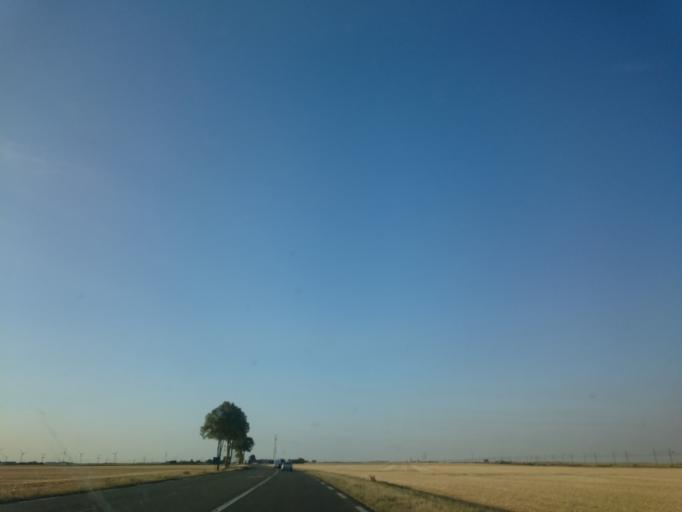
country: FR
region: Centre
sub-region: Departement d'Eure-et-Loir
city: Toury
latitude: 48.2183
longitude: 1.9506
